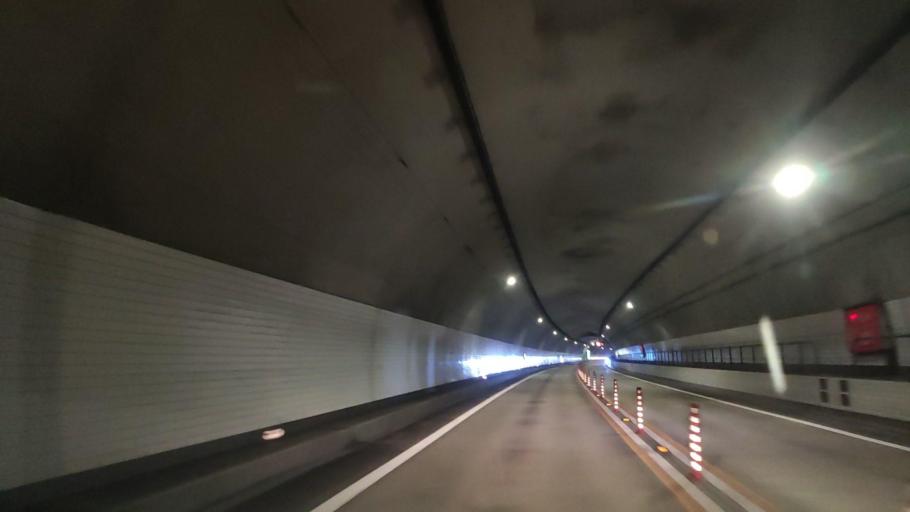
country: JP
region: Kyoto
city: Miyazu
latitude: 35.5546
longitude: 135.1292
